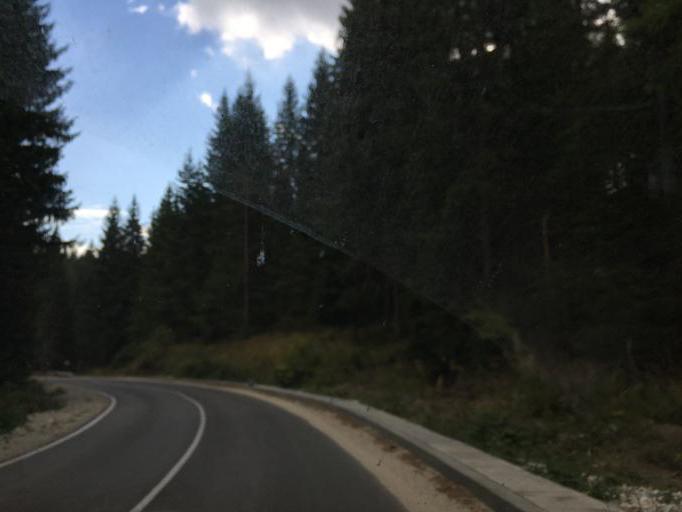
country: BG
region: Pazardzhik
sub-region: Obshtina Batak
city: Batak
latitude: 41.9007
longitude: 24.3065
